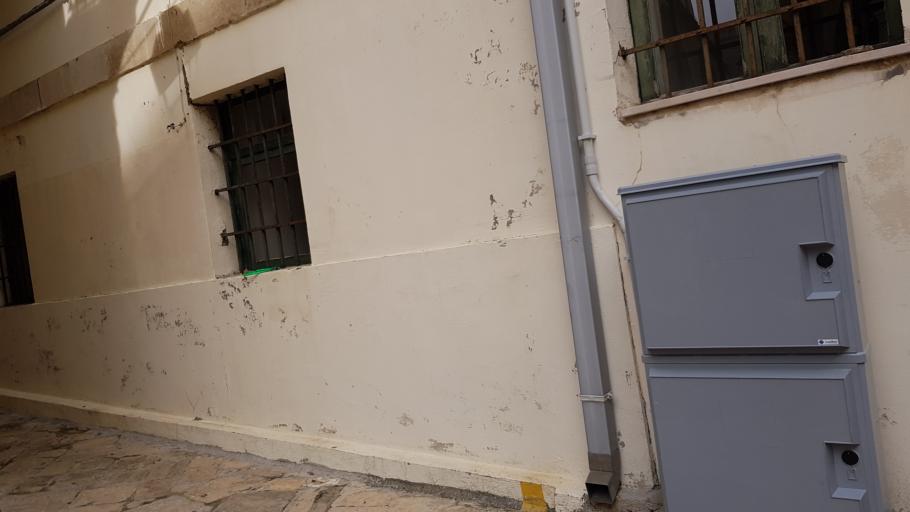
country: IT
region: Apulia
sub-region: Provincia di Lecce
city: Otranto
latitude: 40.1461
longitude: 18.4908
